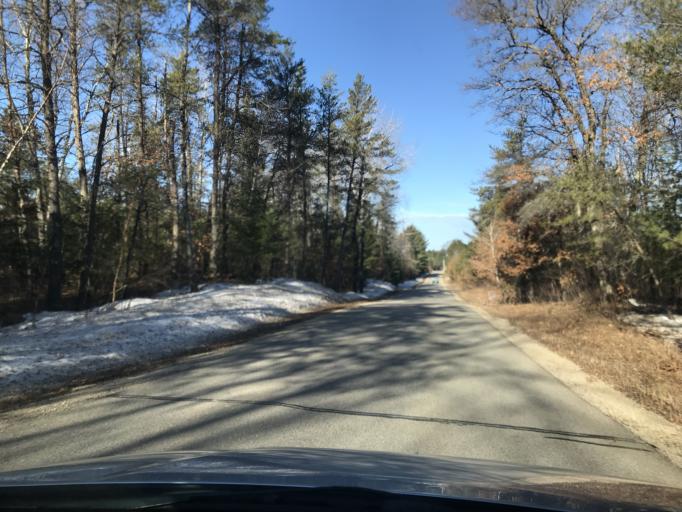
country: US
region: Wisconsin
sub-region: Marinette County
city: Niagara
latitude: 45.3982
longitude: -88.0852
